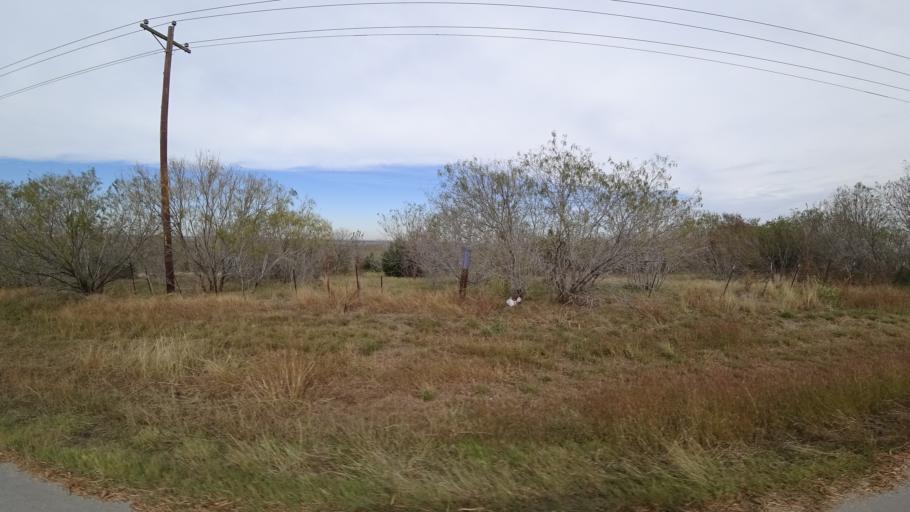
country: US
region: Texas
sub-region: Travis County
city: Garfield
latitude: 30.1488
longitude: -97.5801
